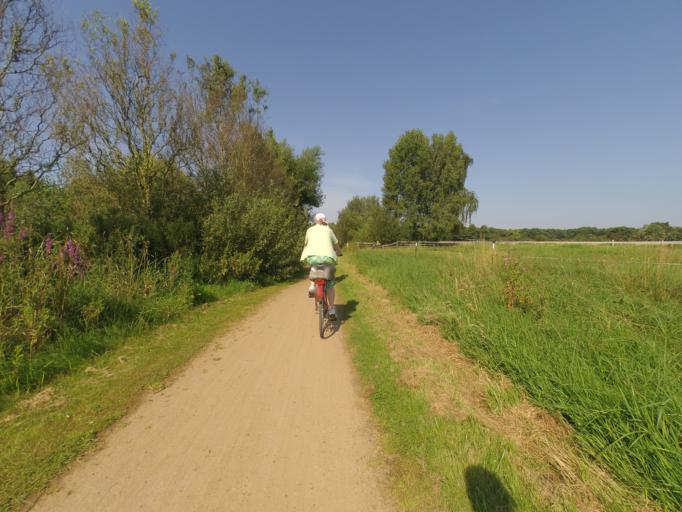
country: DE
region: Schleswig-Holstein
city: Oststeinbek
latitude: 53.5041
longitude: 10.1394
